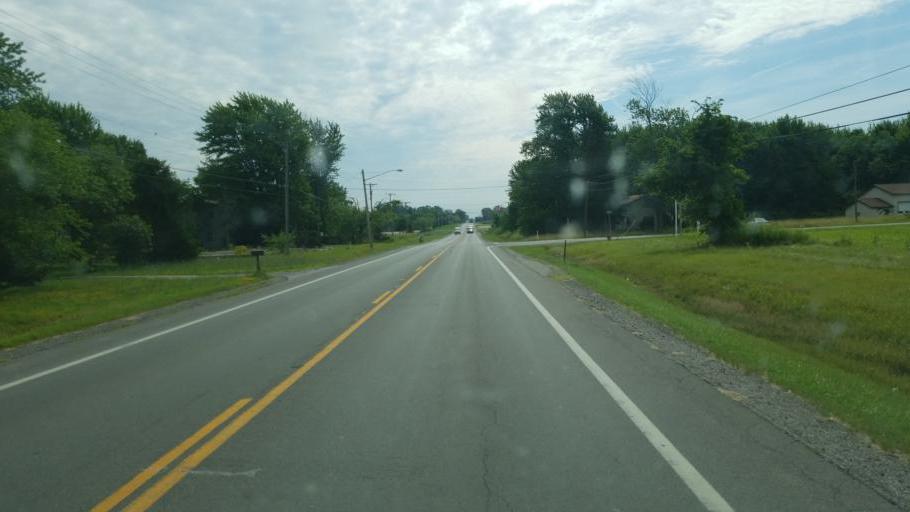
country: US
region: Ohio
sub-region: Lorain County
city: Eaton Estates
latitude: 41.3137
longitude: -81.9921
